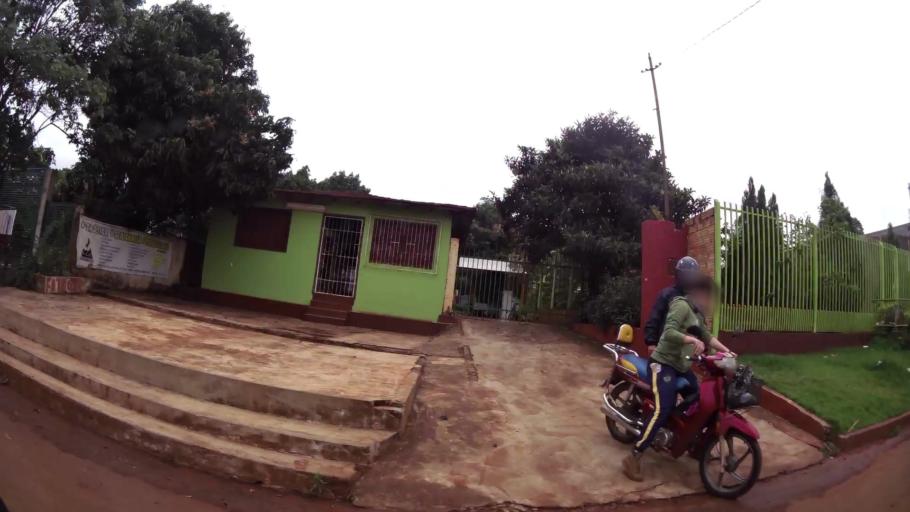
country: PY
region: Alto Parana
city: Presidente Franco
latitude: -25.5052
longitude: -54.6882
